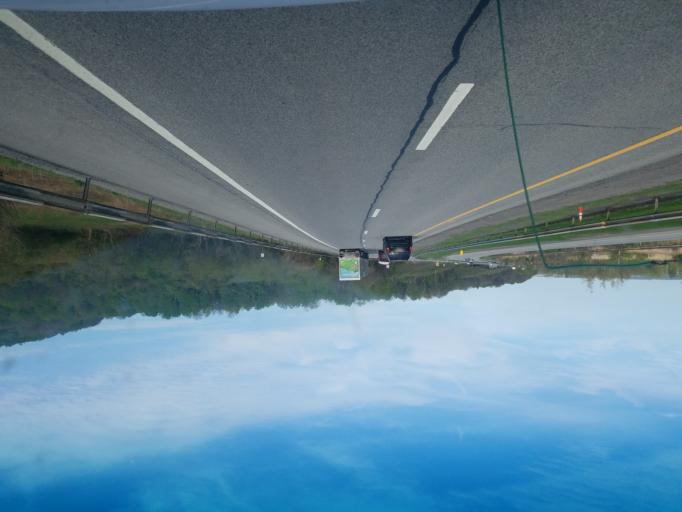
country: US
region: New York
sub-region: Herkimer County
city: Herkimer
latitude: 43.0141
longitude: -74.9755
